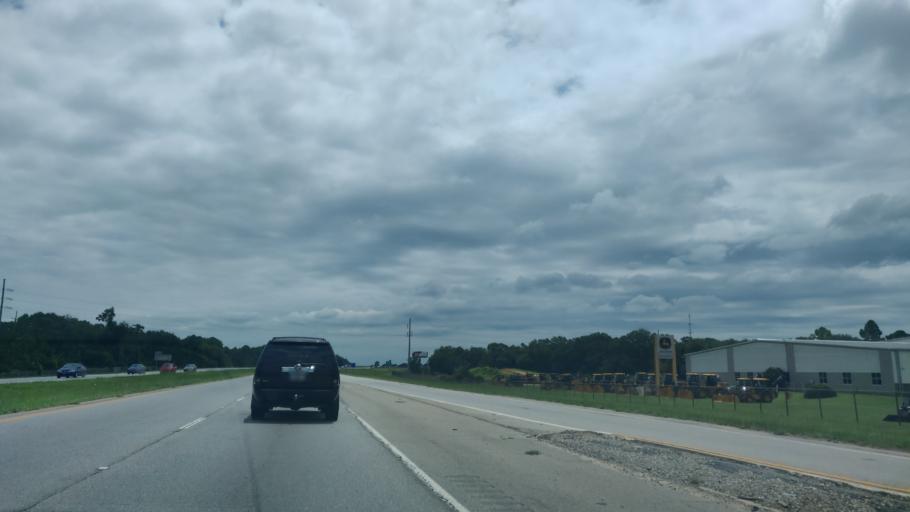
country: US
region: Georgia
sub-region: Dougherty County
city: Albany
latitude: 31.5911
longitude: -84.1225
